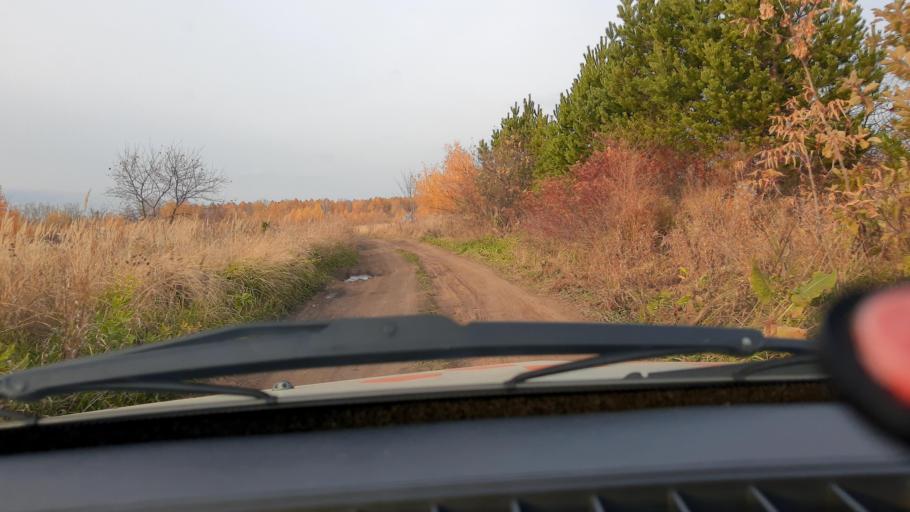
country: RU
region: Bashkortostan
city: Iglino
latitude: 54.8023
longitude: 56.3470
